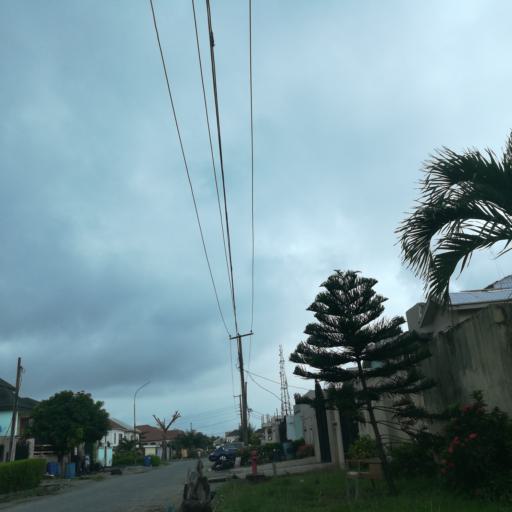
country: NG
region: Lagos
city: Ikoyi
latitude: 6.4382
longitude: 3.4633
